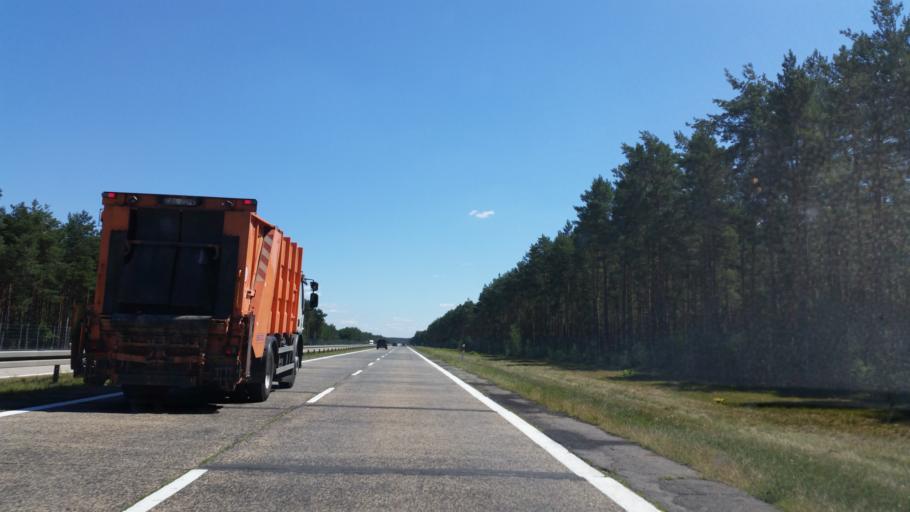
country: PL
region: Lubusz
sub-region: Powiat zaganski
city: Malomice
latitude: 51.4269
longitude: 15.4314
